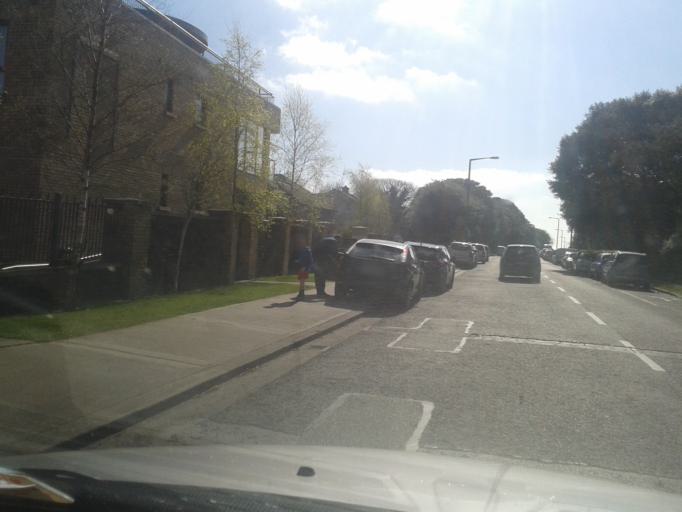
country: IE
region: Leinster
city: Raheny
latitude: 53.3772
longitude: -6.1709
